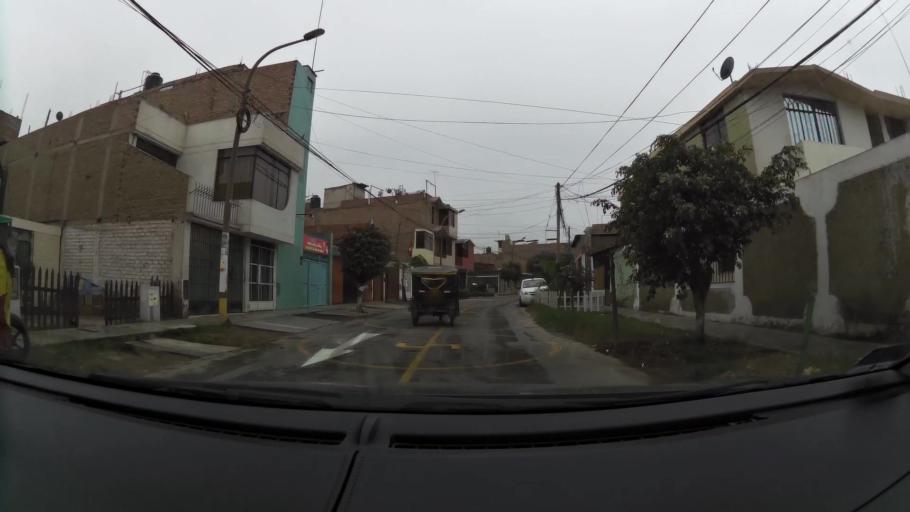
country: PE
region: Lima
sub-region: Lima
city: Independencia
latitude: -11.9658
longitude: -77.0814
